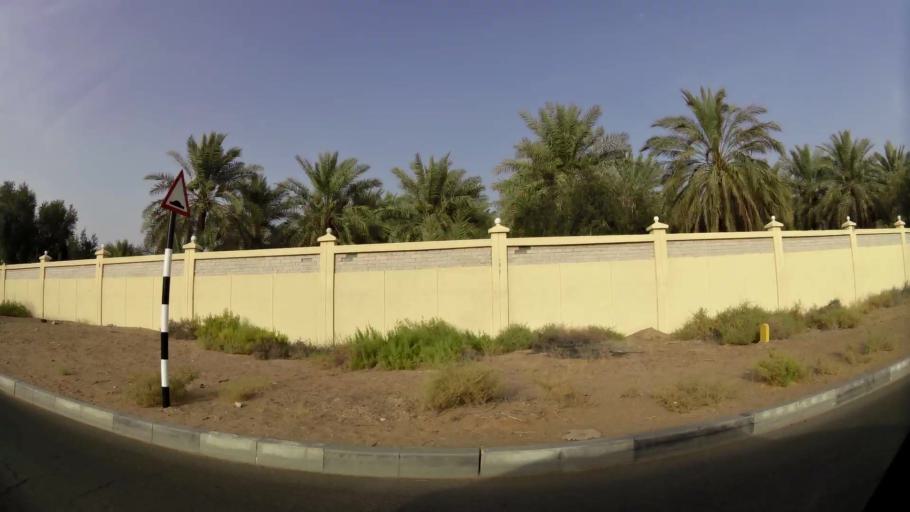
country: AE
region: Abu Dhabi
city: Al Ain
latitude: 24.2409
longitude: 55.7233
